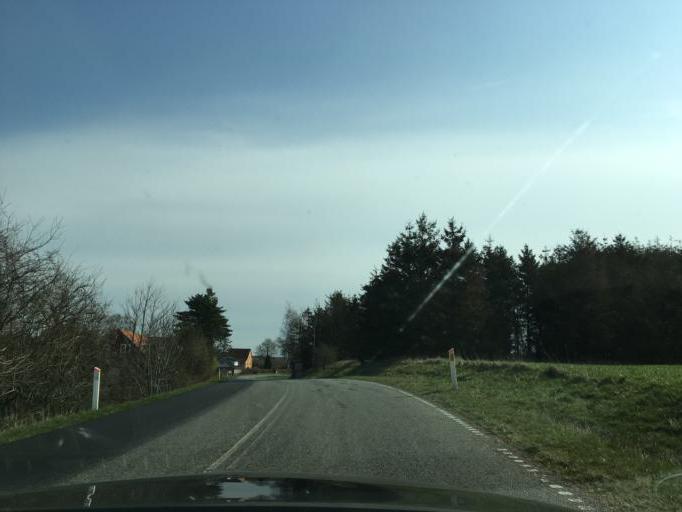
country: DK
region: South Denmark
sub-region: Kolding Kommune
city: Lunderskov
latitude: 55.5073
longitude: 9.3733
